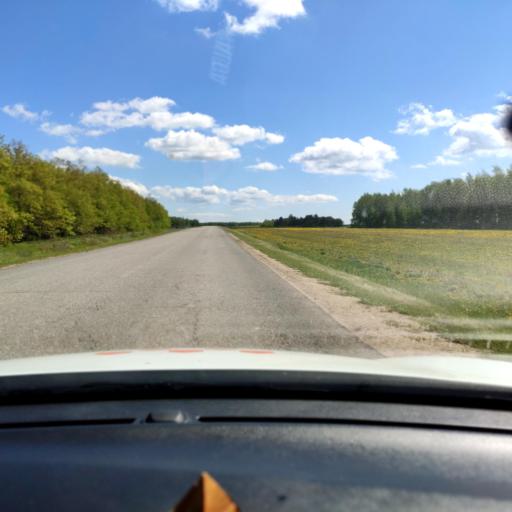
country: RU
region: Tatarstan
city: Kuybyshevskiy Zaton
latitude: 55.3425
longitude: 49.0685
